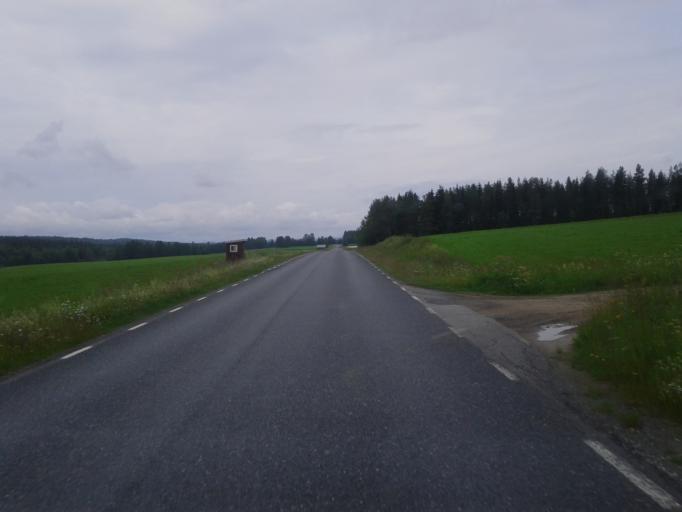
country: SE
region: Vaesterbotten
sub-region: Skelleftea Kommun
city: Viken
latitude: 64.8904
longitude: 20.7354
